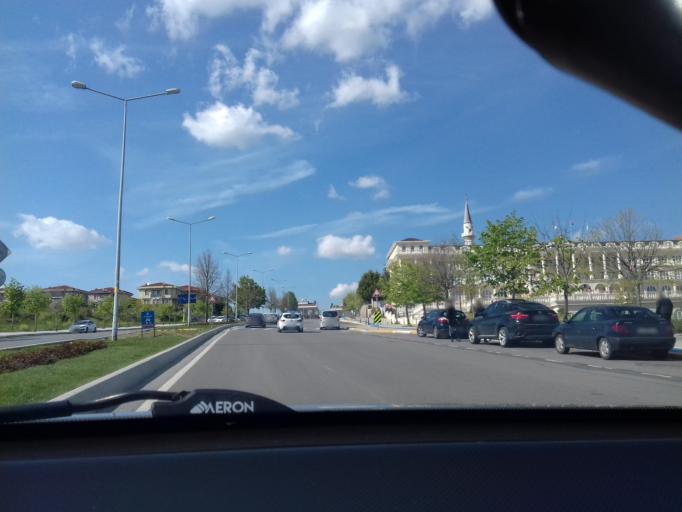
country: TR
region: Istanbul
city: Sultanbeyli
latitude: 40.9277
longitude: 29.2836
